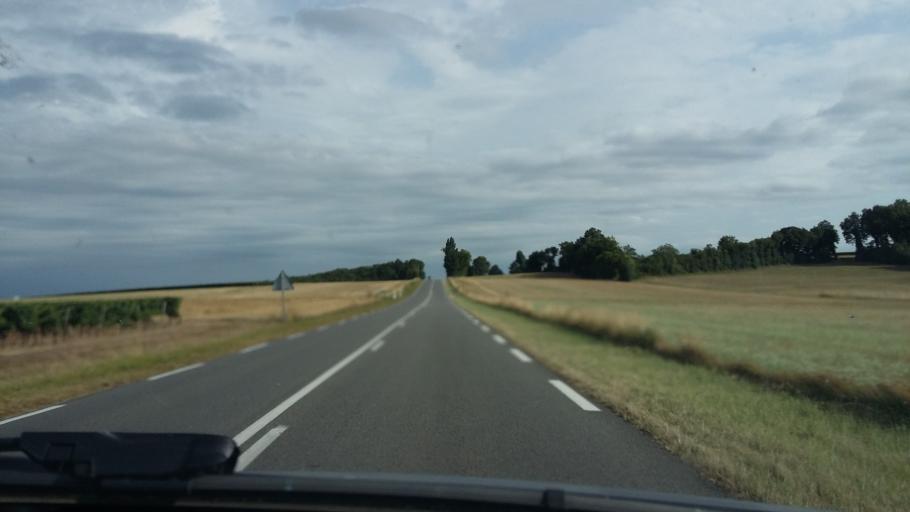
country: FR
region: Poitou-Charentes
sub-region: Departement de la Charente
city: Asnieres-sur-Nouere
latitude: 45.7197
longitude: 0.0722
